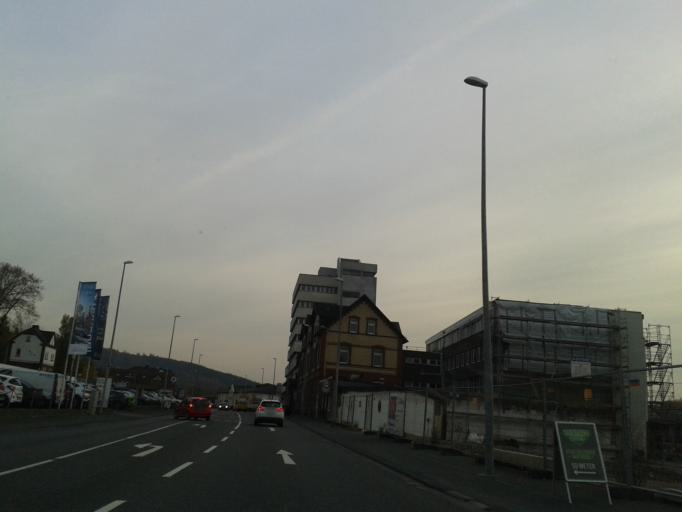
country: DE
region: Hesse
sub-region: Regierungsbezirk Giessen
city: Sinn
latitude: 50.6586
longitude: 8.3260
